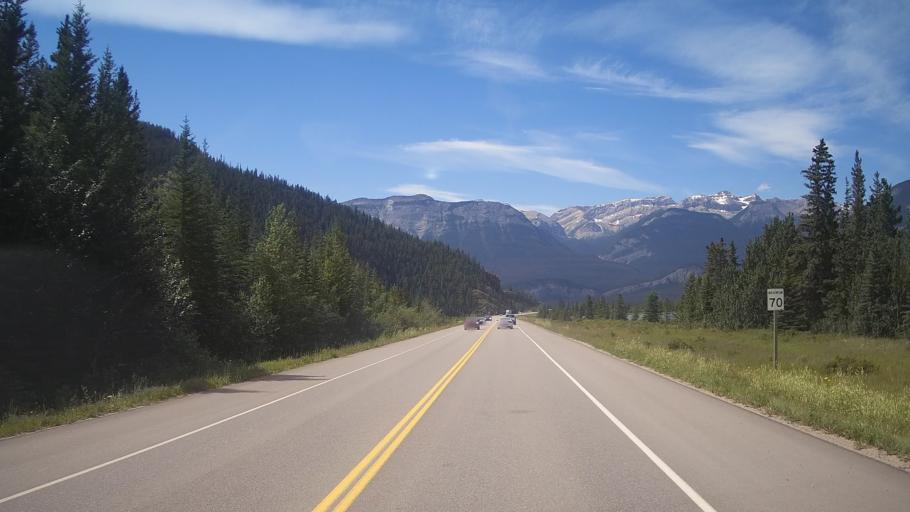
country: CA
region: Alberta
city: Jasper Park Lodge
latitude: 53.0511
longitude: -118.0732
